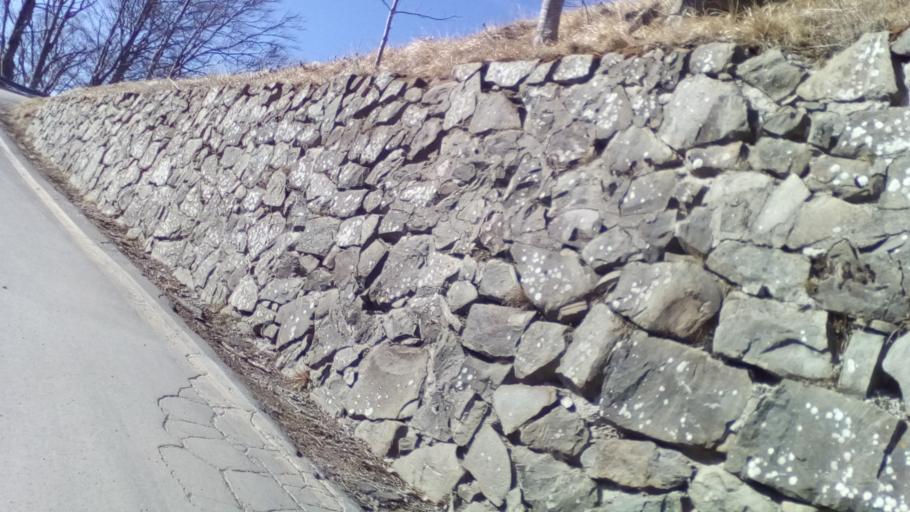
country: IT
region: Tuscany
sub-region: Provincia di Lucca
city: Fosciandora
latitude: 44.1882
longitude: 10.4797
